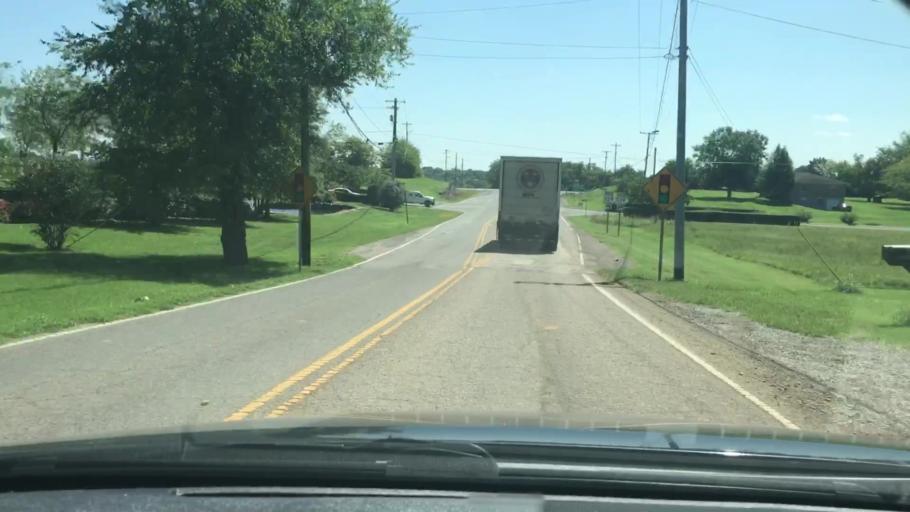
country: US
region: Tennessee
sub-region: Sumner County
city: Gallatin
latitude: 36.3992
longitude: -86.4823
